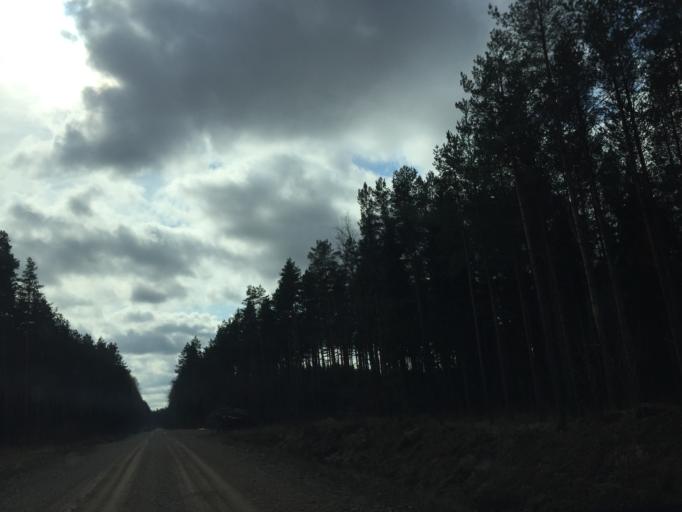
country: LV
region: Vecumnieki
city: Vecumnieki
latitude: 56.5976
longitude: 24.6397
